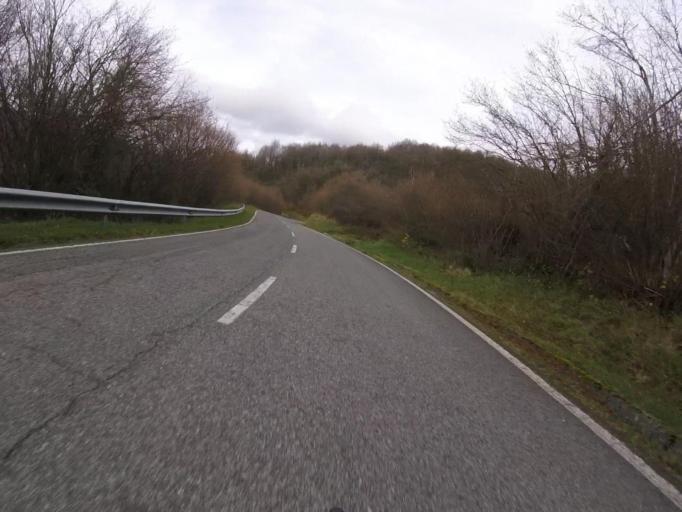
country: ES
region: Navarre
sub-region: Provincia de Navarra
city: Olazagutia
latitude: 42.8718
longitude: -2.1832
